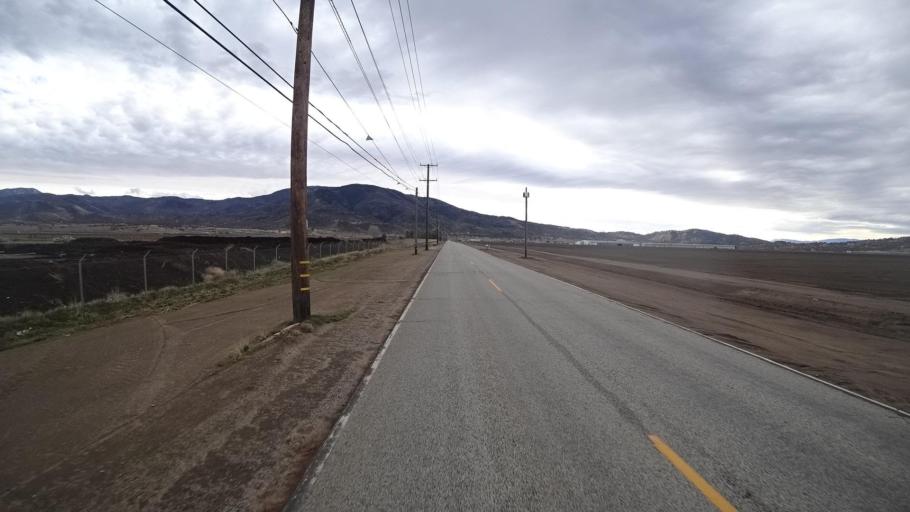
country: US
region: California
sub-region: Kern County
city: Stallion Springs
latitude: 35.1134
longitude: -118.6018
